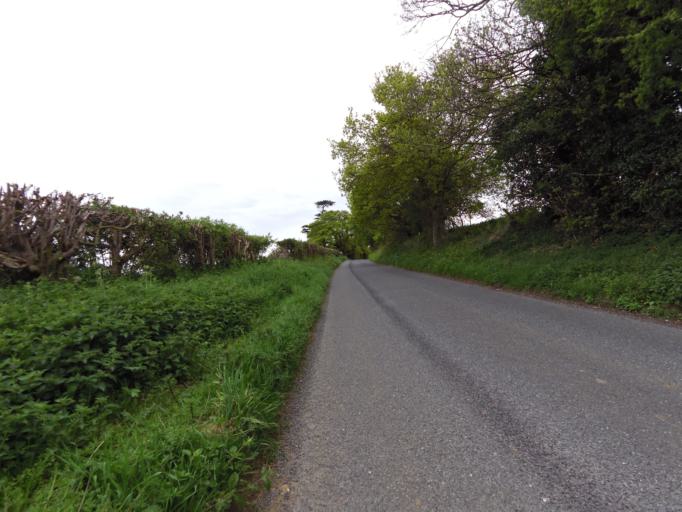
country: GB
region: England
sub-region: Suffolk
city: Kesgrave
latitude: 52.0103
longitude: 1.2404
